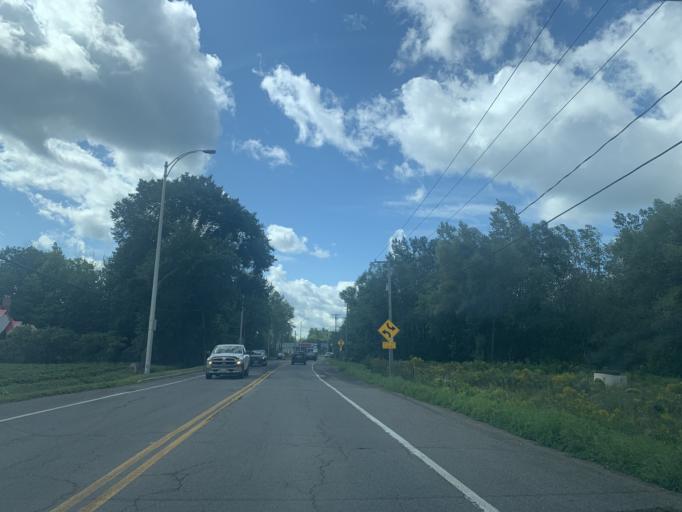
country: CA
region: Ontario
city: Hawkesbury
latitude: 45.6295
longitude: -74.5893
